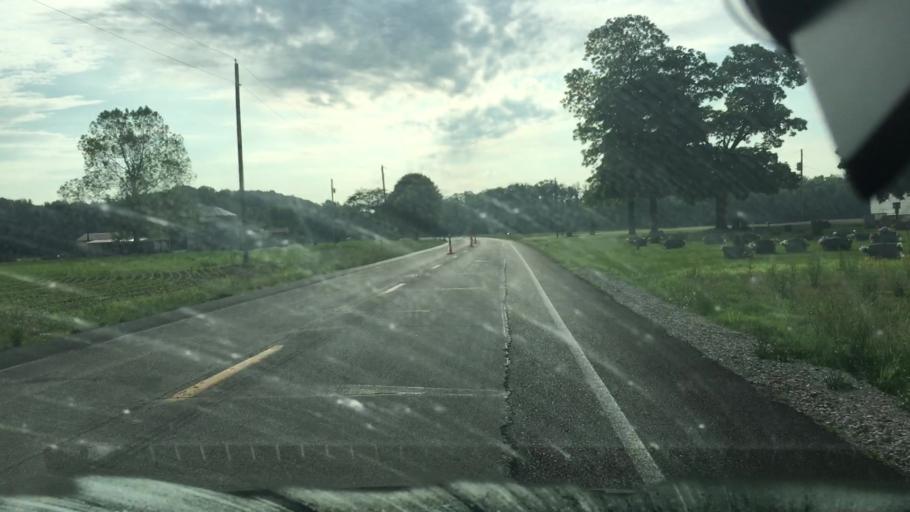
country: US
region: Kentucky
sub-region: Hancock County
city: Lewisport
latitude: 37.9507
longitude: -86.9550
